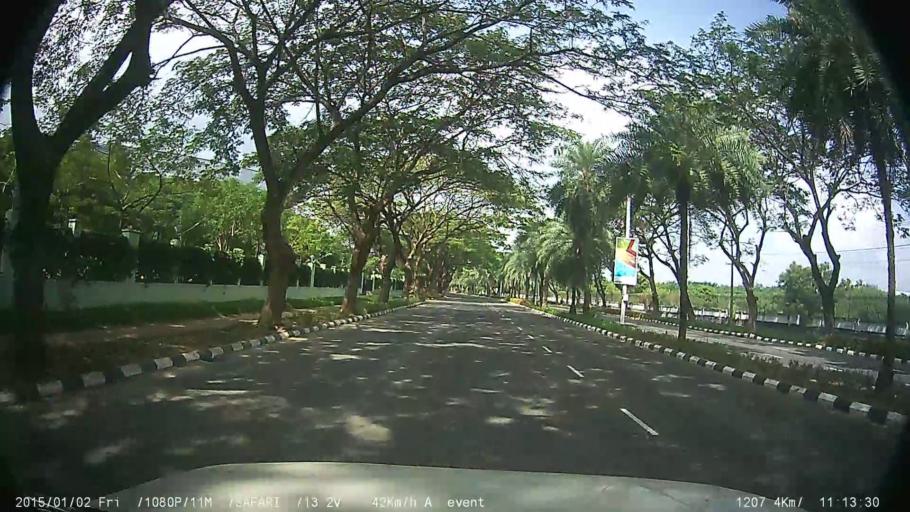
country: IN
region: Tamil Nadu
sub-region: Kancheepuram
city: Singapperumalkovil
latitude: 12.7344
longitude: 80.0105
